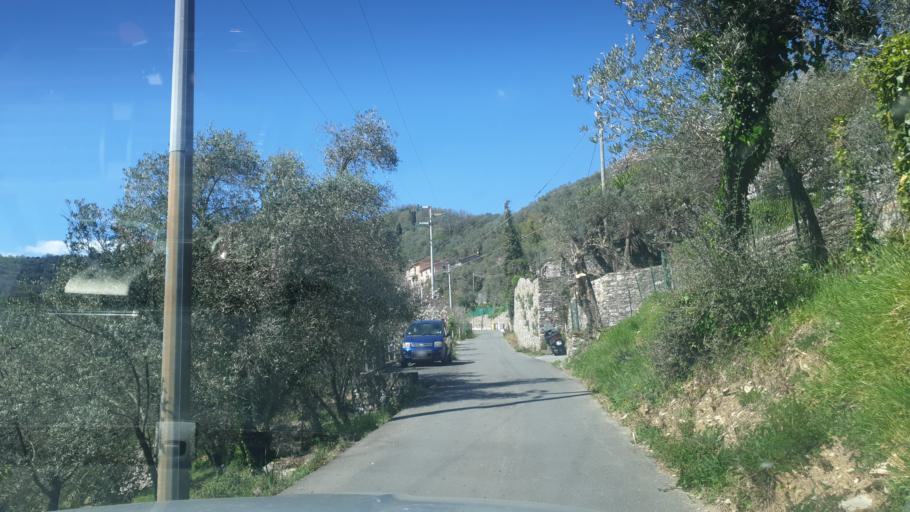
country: IT
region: Liguria
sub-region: Provincia di Genova
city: Avegno
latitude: 44.3795
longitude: 9.1468
